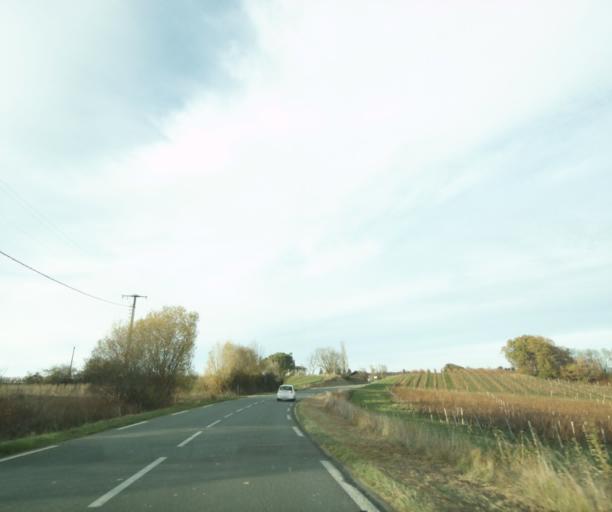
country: FR
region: Midi-Pyrenees
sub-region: Departement du Gers
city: Eauze
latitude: 43.8061
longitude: 0.0967
